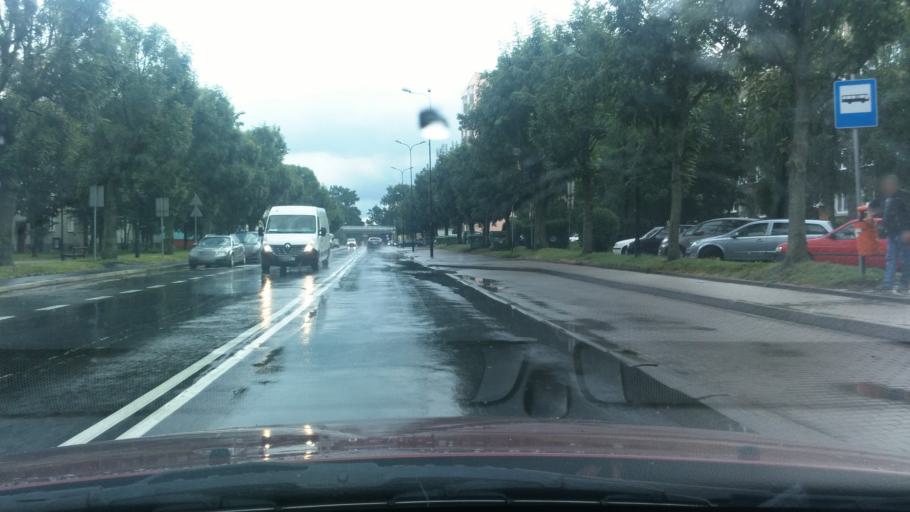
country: PL
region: Lower Silesian Voivodeship
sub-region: Powiat zgorzelecki
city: Zgorzelec
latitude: 51.1441
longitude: 15.0098
